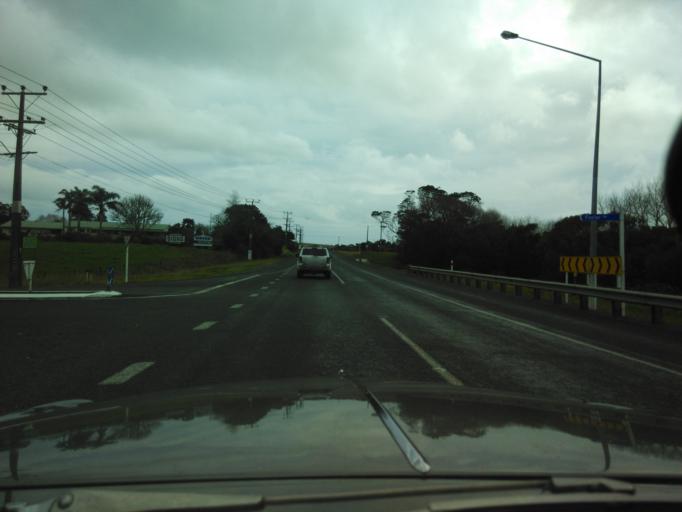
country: NZ
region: Auckland
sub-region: Auckland
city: Muriwai Beach
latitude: -36.7666
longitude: 174.5126
